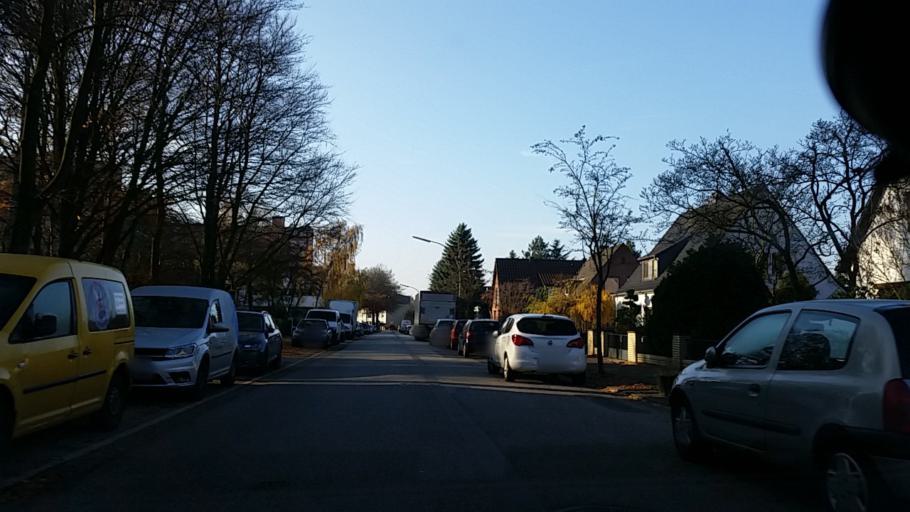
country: DE
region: Schleswig-Holstein
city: Oststeinbek
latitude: 53.5365
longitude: 10.1337
